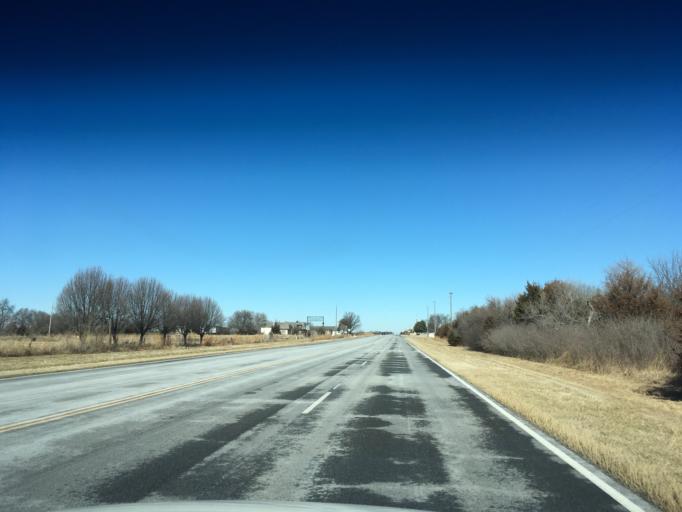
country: US
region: Kansas
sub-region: Harvey County
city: Newton
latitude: 37.9536
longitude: -97.3364
